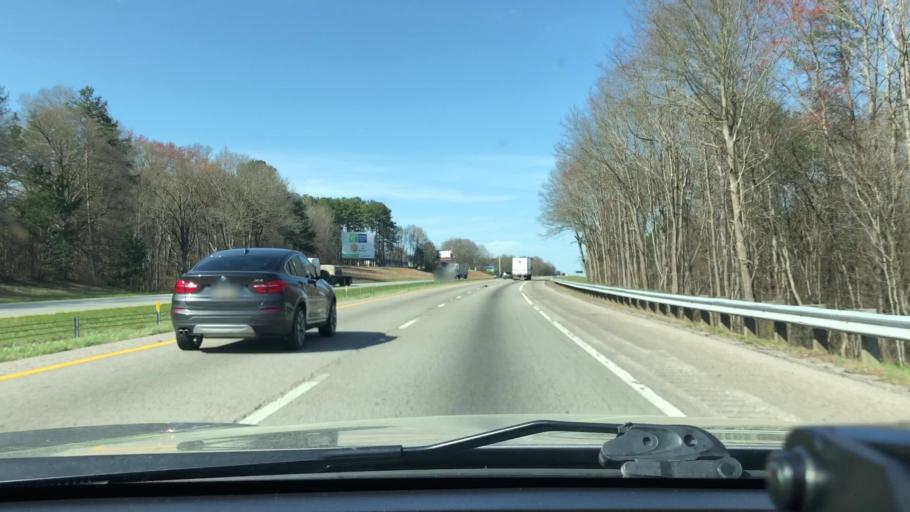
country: US
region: South Carolina
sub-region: Spartanburg County
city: Roebuck
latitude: 34.8876
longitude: -81.9934
